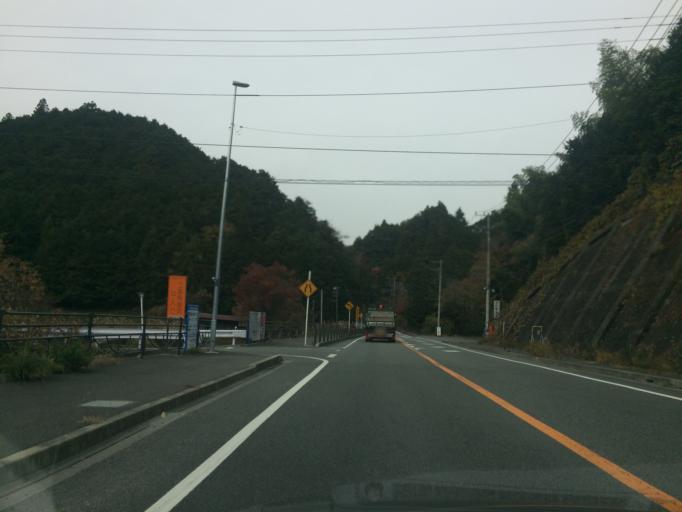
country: JP
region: Shizuoka
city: Fujinomiya
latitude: 35.2668
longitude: 138.4605
